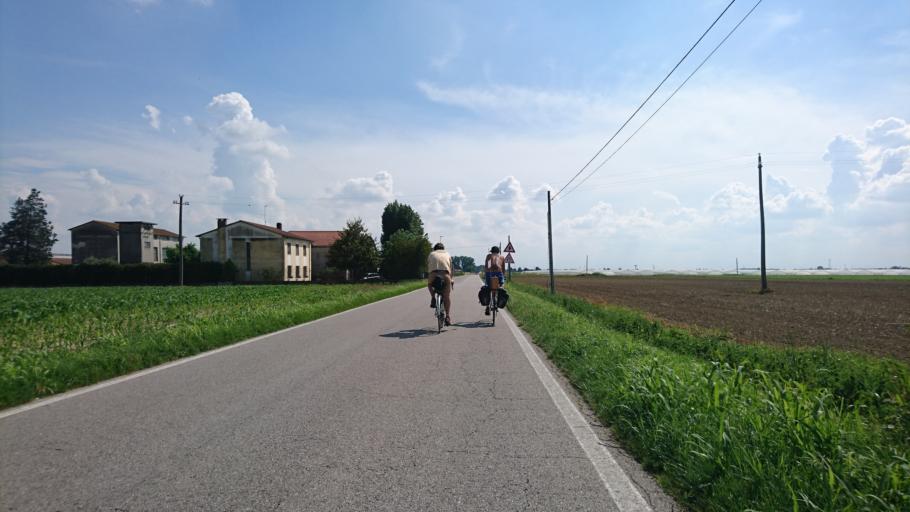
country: IT
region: Veneto
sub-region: Provincia di Rovigo
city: Castelmassa
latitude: 45.0520
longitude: 11.3258
